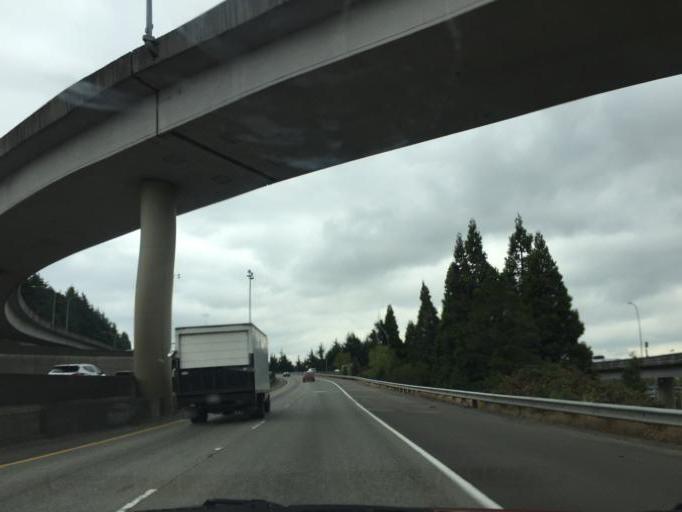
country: US
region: Washington
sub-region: King County
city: Seattle
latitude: 47.5929
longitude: -122.3213
